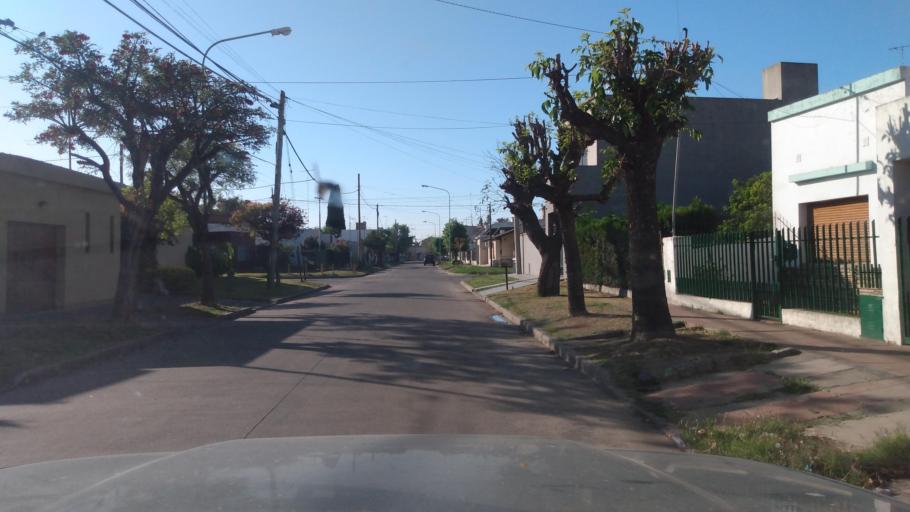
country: AR
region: Buenos Aires
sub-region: Partido de Lujan
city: Lujan
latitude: -34.5575
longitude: -59.1121
